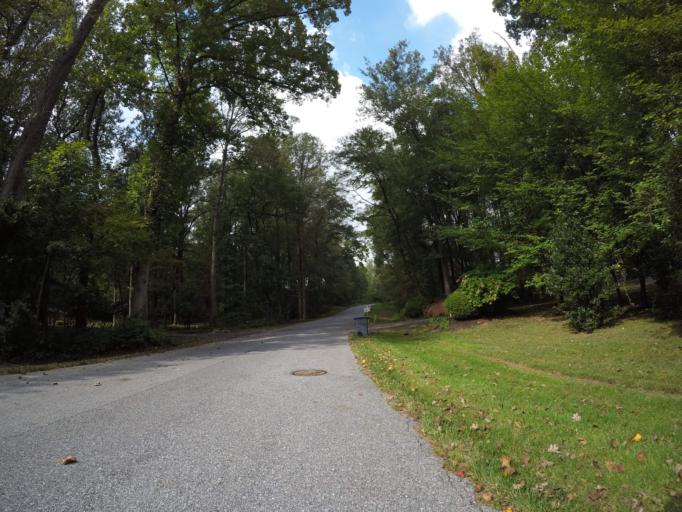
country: US
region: Maryland
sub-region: Howard County
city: Columbia
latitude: 39.2598
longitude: -76.8797
